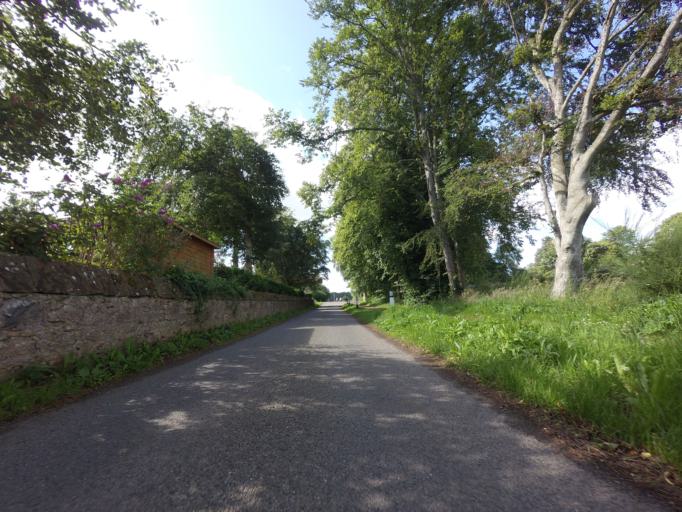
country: GB
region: Scotland
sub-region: Highland
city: Nairn
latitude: 57.5741
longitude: -3.8631
